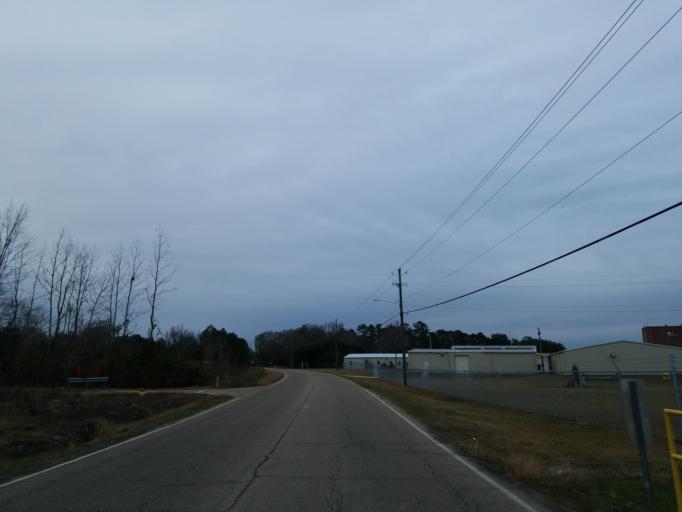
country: US
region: Mississippi
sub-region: Forrest County
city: Hattiesburg
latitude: 31.3135
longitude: -89.2818
